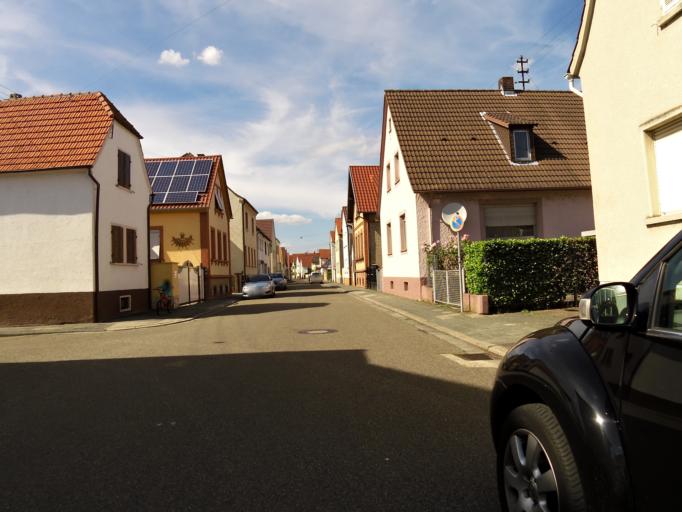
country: DE
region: Rheinland-Pfalz
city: Bohl-Iggelheim
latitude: 49.3639
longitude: 8.3042
